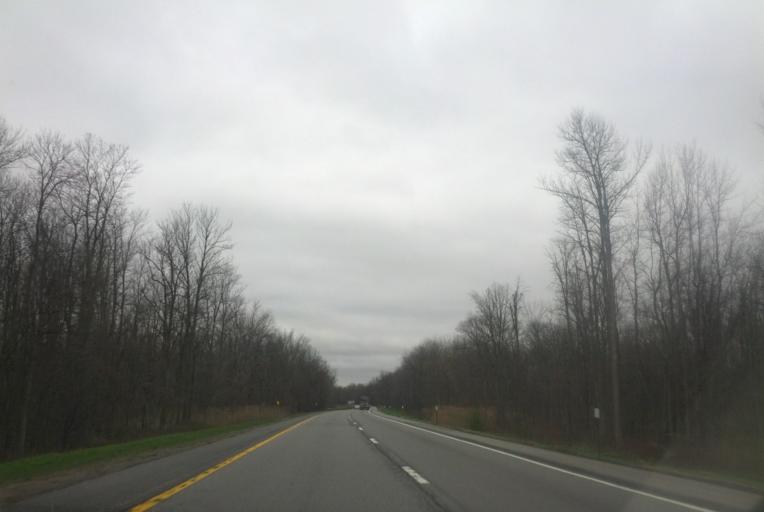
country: US
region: New York
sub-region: Ontario County
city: Shortsville
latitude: 42.9751
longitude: -77.1847
